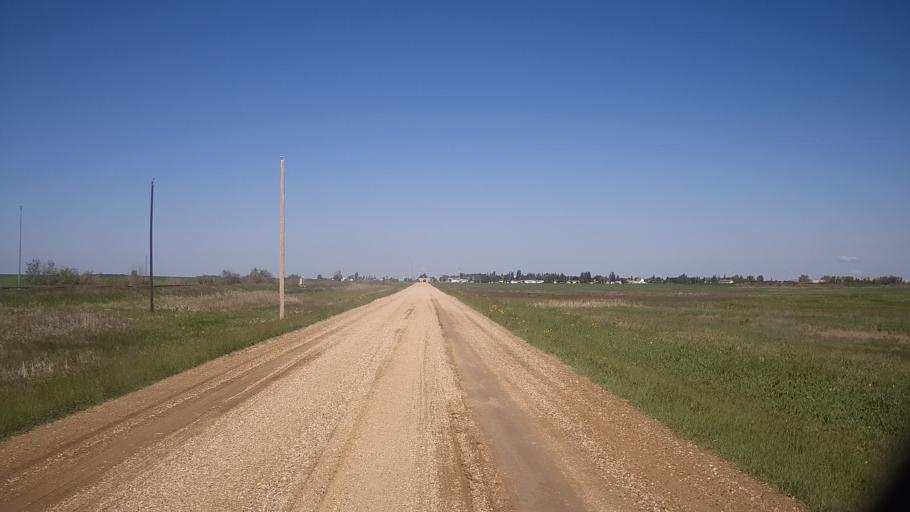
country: CA
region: Saskatchewan
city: Watrous
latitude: 51.8860
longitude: -106.0371
